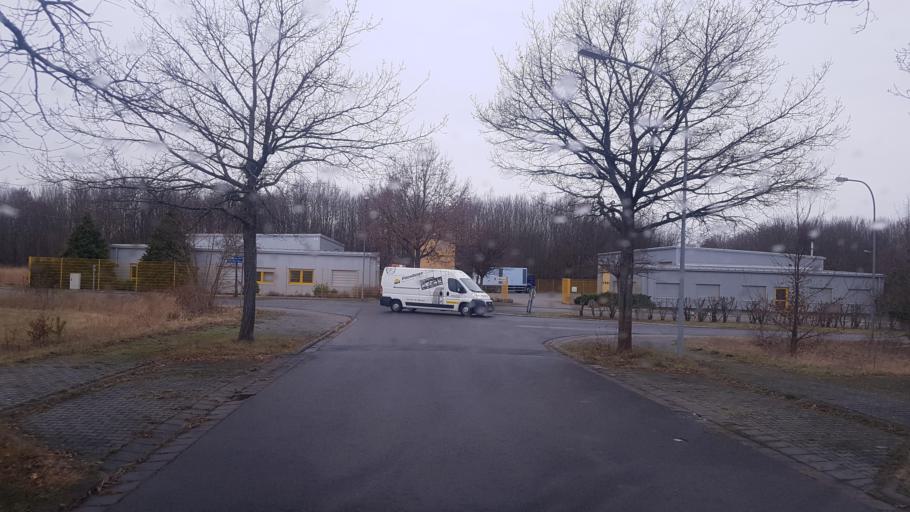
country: DE
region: Brandenburg
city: Schwarzheide
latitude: 51.4722
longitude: 13.8266
